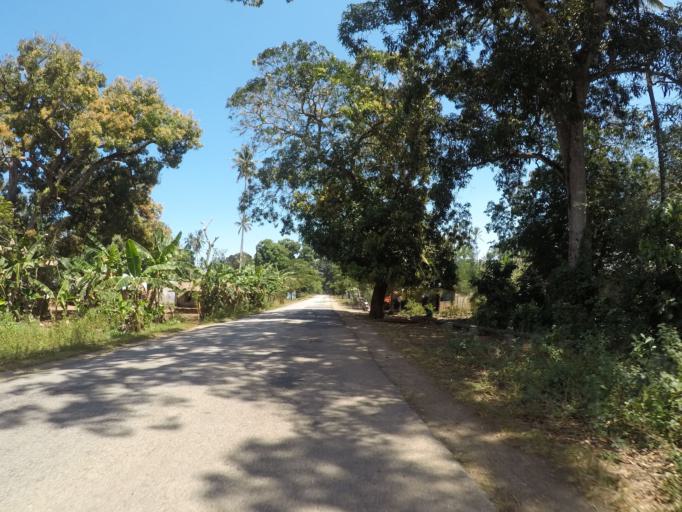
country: TZ
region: Zanzibar Central/South
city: Nganane
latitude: -6.2938
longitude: 39.4378
